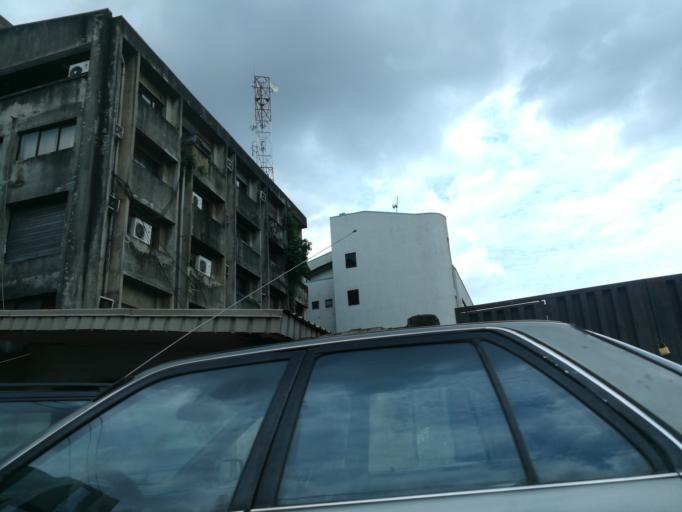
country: NG
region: Lagos
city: Ikeja
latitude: 6.5971
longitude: 3.3490
